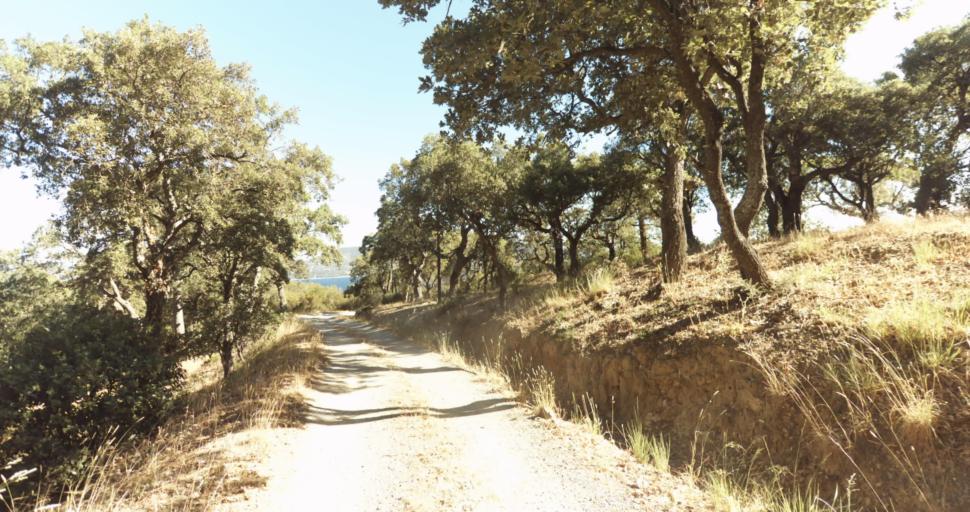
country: FR
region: Provence-Alpes-Cote d'Azur
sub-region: Departement du Var
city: Saint-Tropez
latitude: 43.2553
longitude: 6.6213
